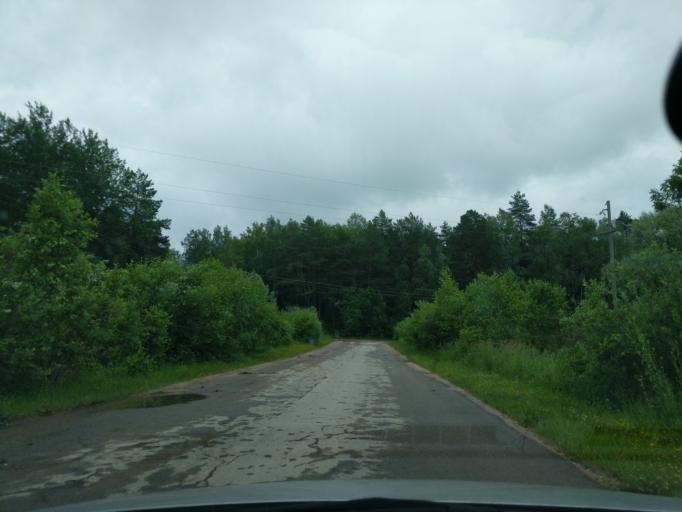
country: RU
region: Kaluga
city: Myatlevo
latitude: 54.8267
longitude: 35.6697
